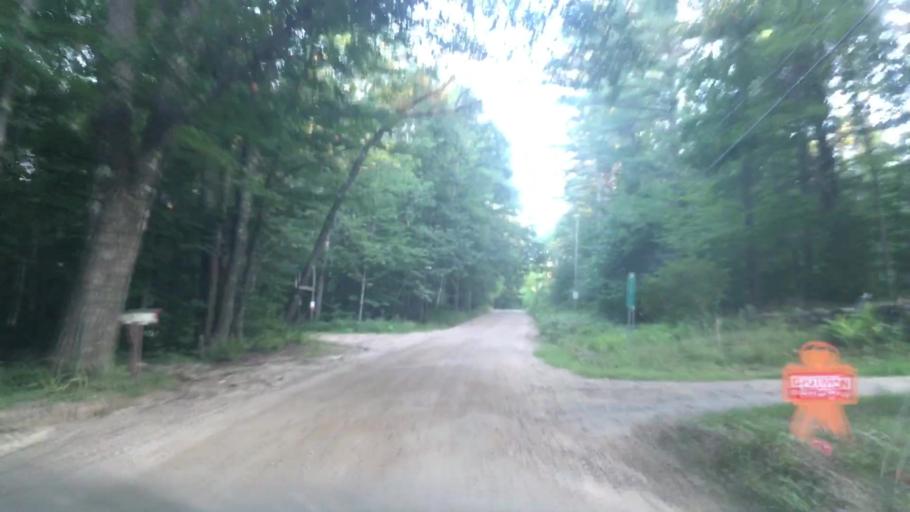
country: US
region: New Hampshire
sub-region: Belknap County
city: Barnstead
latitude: 43.4157
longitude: -71.2844
